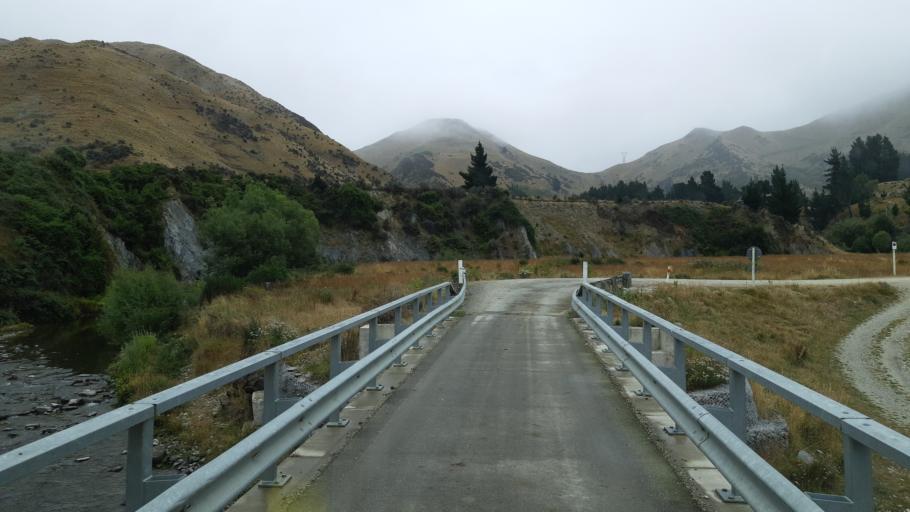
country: NZ
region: Otago
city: Oamaru
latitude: -44.9562
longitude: 170.4808
